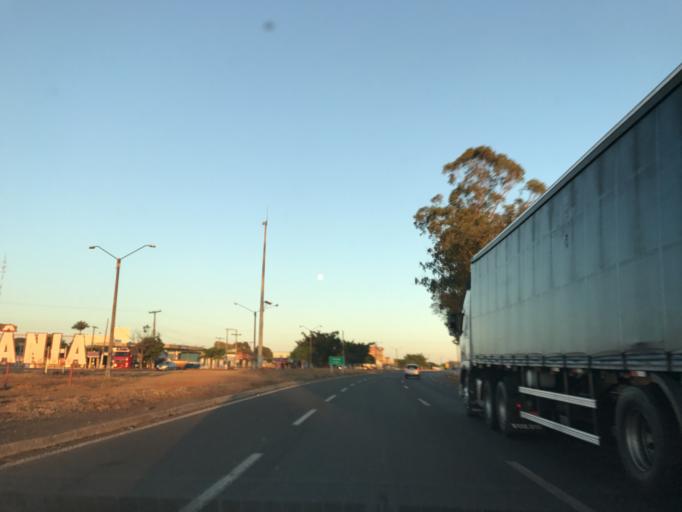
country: BR
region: Goias
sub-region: Abadiania
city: Abadiania
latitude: -16.1914
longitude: -48.7064
